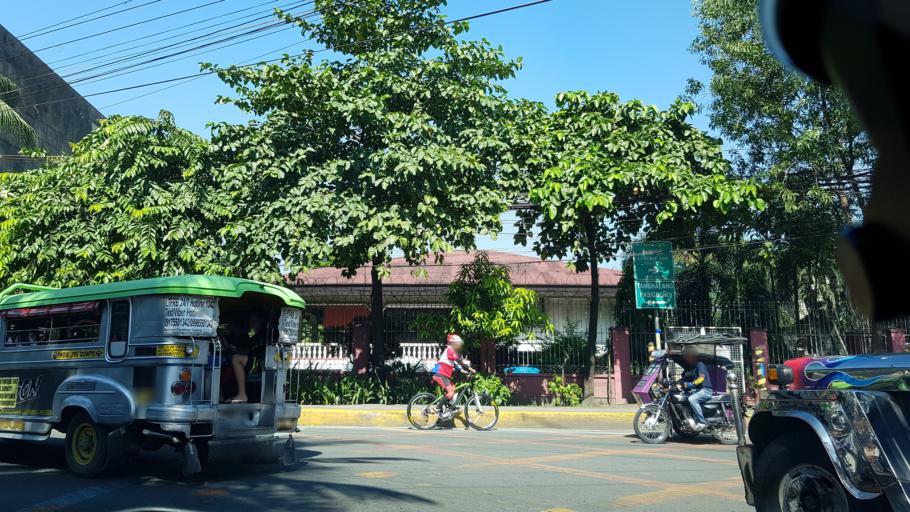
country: PH
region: Calabarzon
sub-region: Province of Rizal
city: Pateros
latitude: 14.5606
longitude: 121.0810
